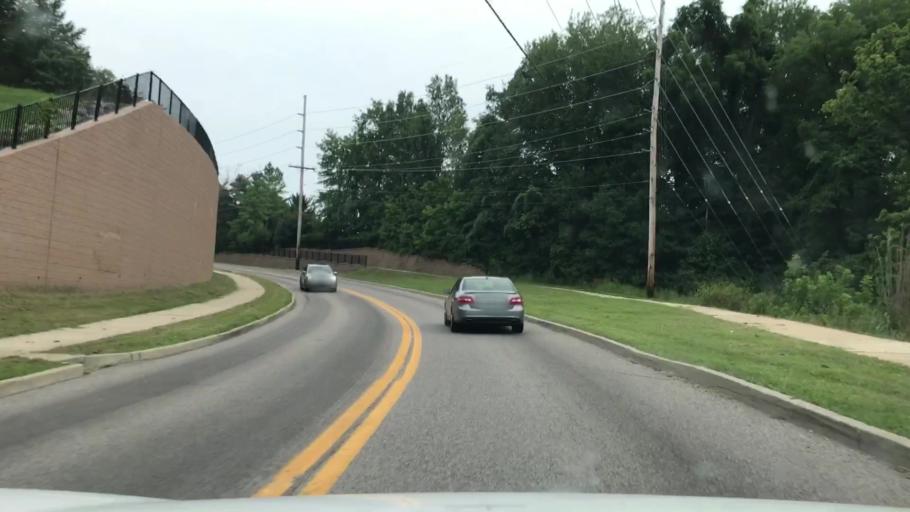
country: US
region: Missouri
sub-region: Saint Louis County
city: Chesterfield
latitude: 38.6561
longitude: -90.6186
